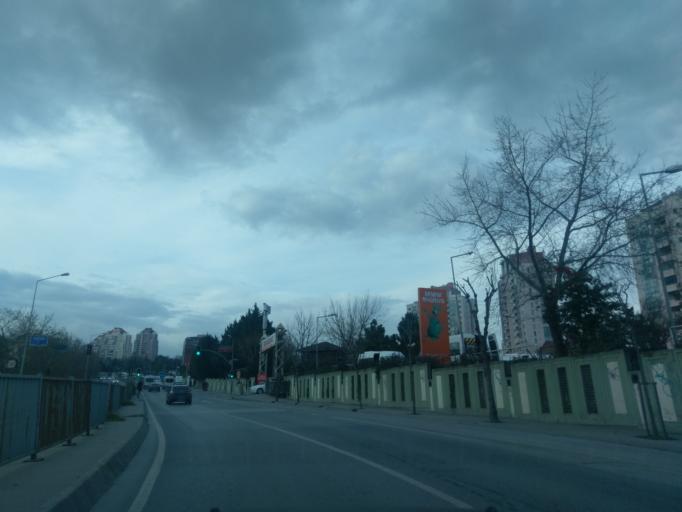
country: TR
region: Istanbul
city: Esenyurt
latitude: 41.0614
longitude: 28.6861
